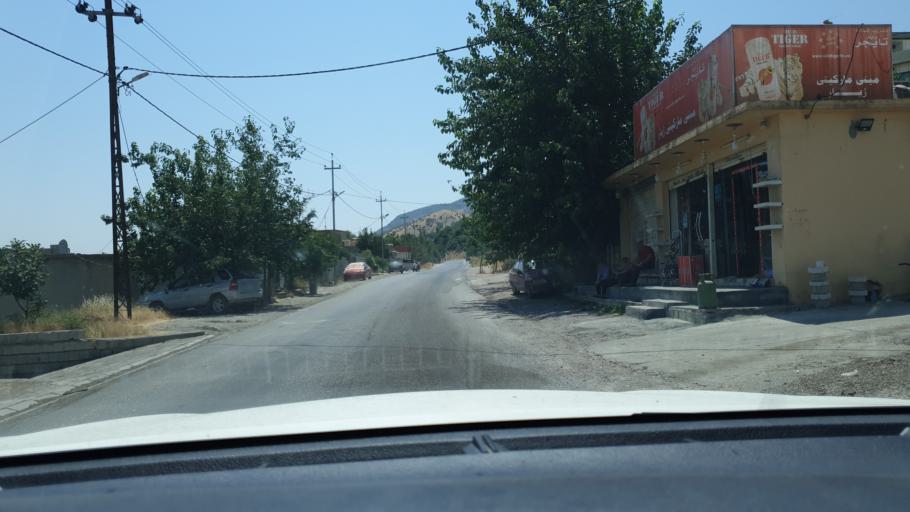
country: IQ
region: Arbil
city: Nahiyat Hiran
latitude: 36.2957
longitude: 44.4743
